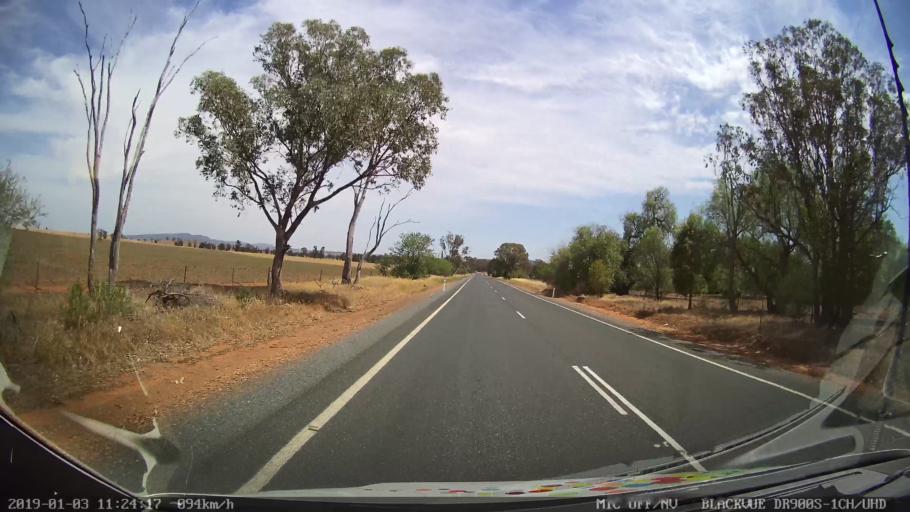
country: AU
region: New South Wales
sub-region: Weddin
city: Grenfell
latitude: -34.0534
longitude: 148.2360
